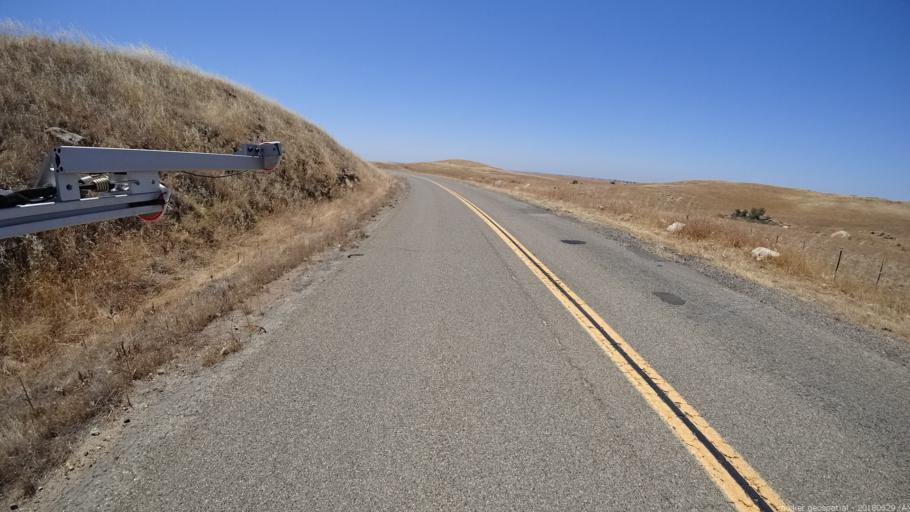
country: US
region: California
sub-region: Madera County
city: Bonadelle Ranchos-Madera Ranchos
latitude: 37.0920
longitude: -119.8816
